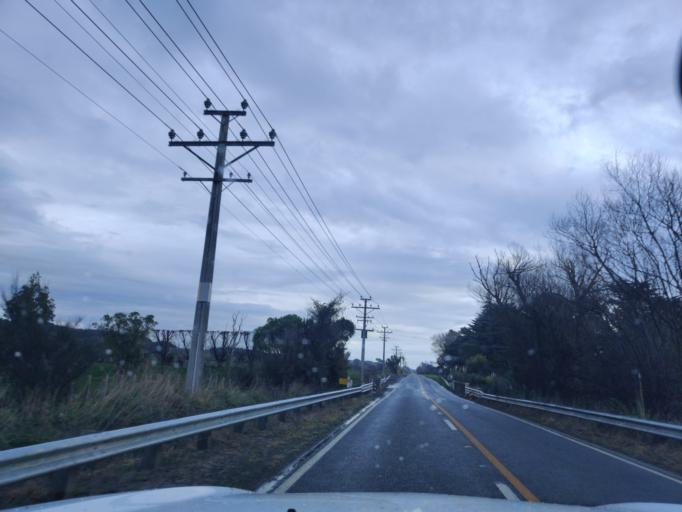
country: NZ
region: Manawatu-Wanganui
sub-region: Palmerston North City
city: Palmerston North
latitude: -40.3439
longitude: 175.7115
